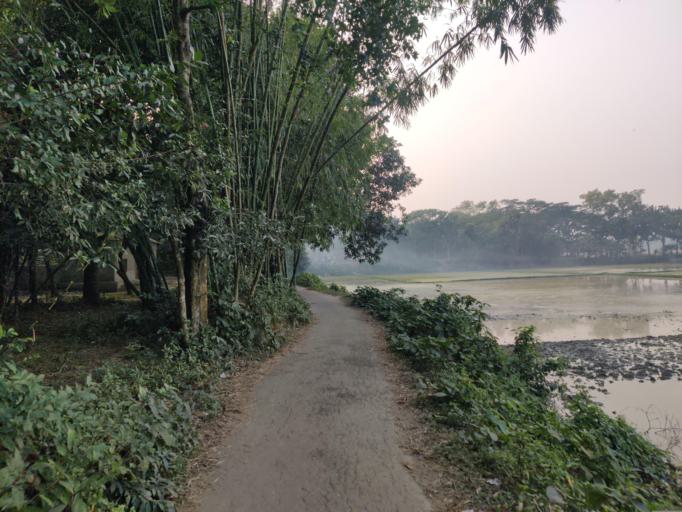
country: BD
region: Dhaka
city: Bajitpur
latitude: 24.1550
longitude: 90.7629
